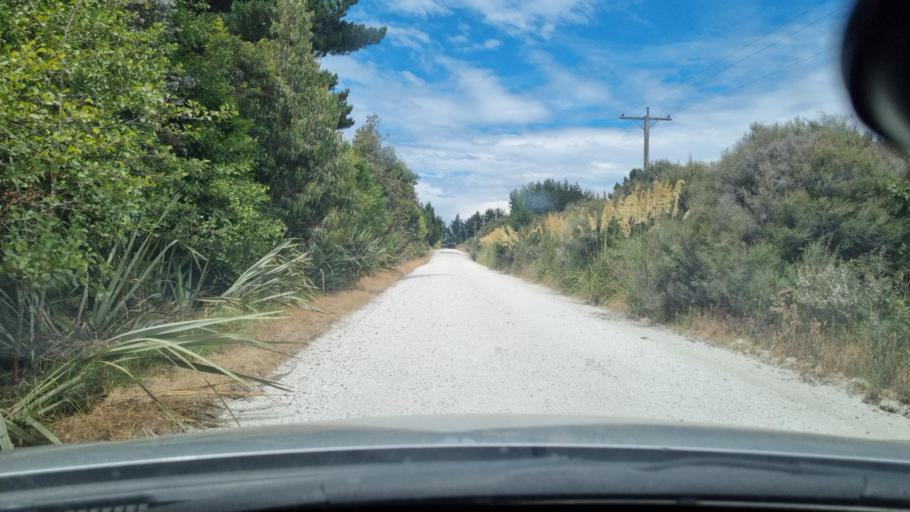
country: NZ
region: Southland
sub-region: Invercargill City
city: Bluff
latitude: -46.5566
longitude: 168.4336
